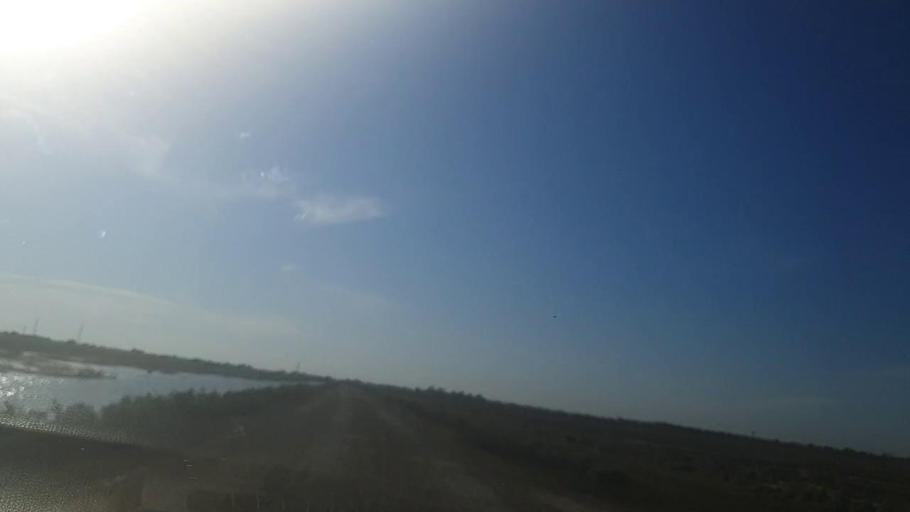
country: PK
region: Sindh
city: Pithoro
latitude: 25.5109
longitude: 69.4036
